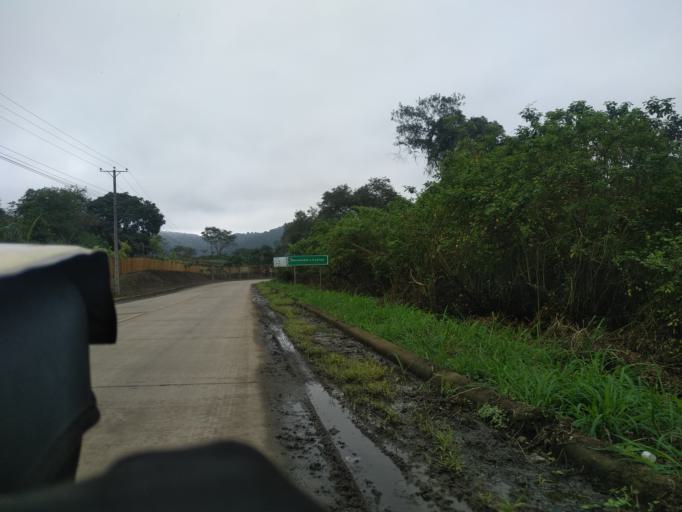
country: EC
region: Manabi
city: Jipijapa
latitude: -1.6695
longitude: -80.8089
